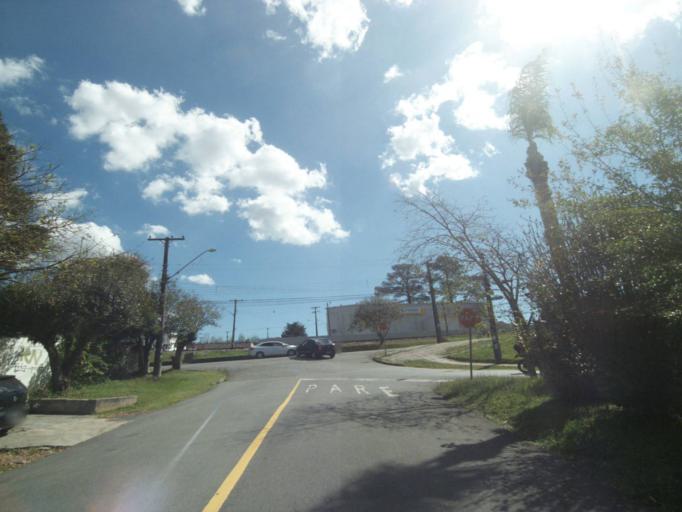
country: BR
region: Parana
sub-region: Curitiba
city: Curitiba
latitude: -25.3852
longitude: -49.2606
